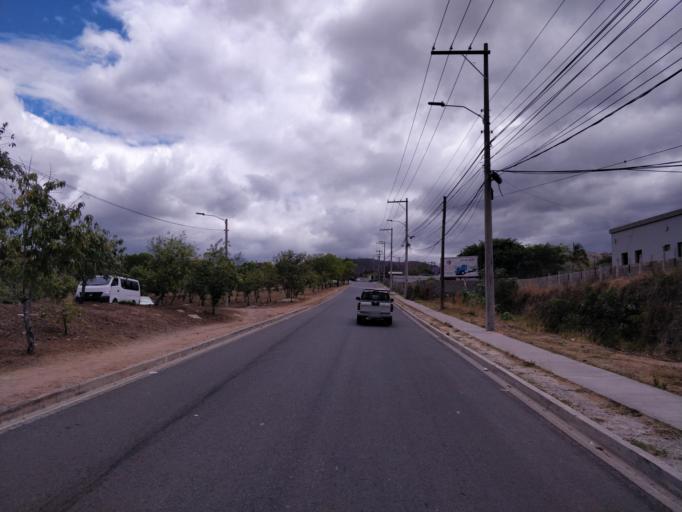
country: HN
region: Francisco Morazan
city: Yaguacire
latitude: 14.0442
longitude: -87.2248
